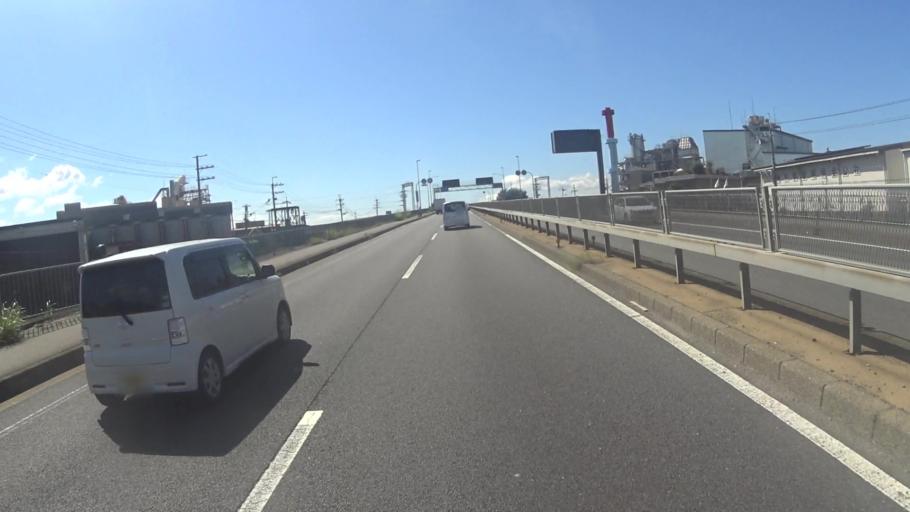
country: JP
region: Kyoto
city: Muko
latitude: 34.9221
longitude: 135.7447
